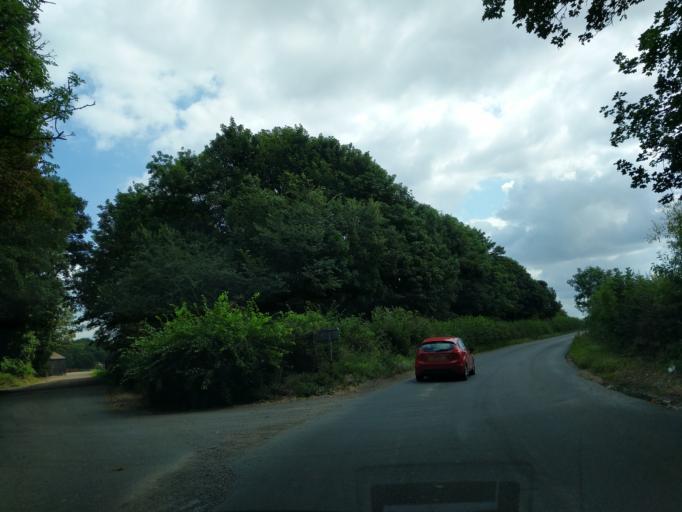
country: GB
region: England
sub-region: Cambridgeshire
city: Isleham
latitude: 52.2932
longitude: 0.4518
